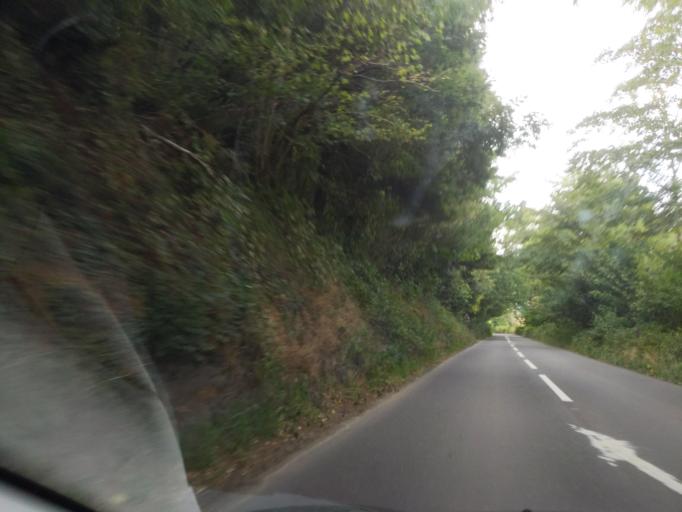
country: GB
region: England
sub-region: Devon
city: Winkleigh
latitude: 50.9635
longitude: -3.9655
